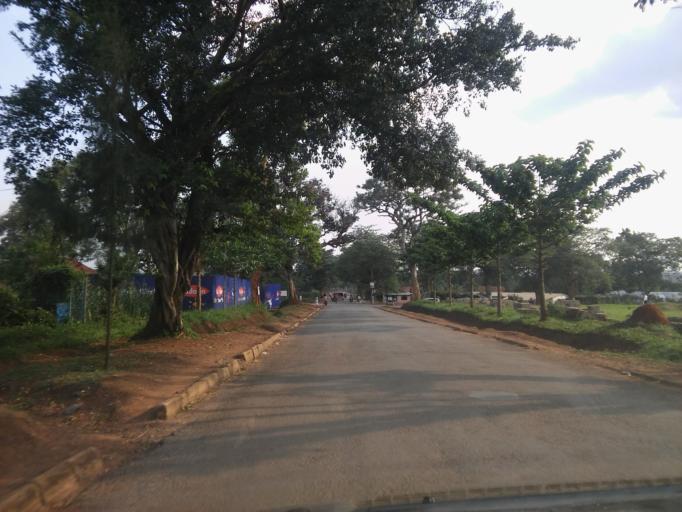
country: UG
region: Eastern Region
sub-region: Mbale District
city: Mbale
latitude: 1.0696
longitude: 34.1828
